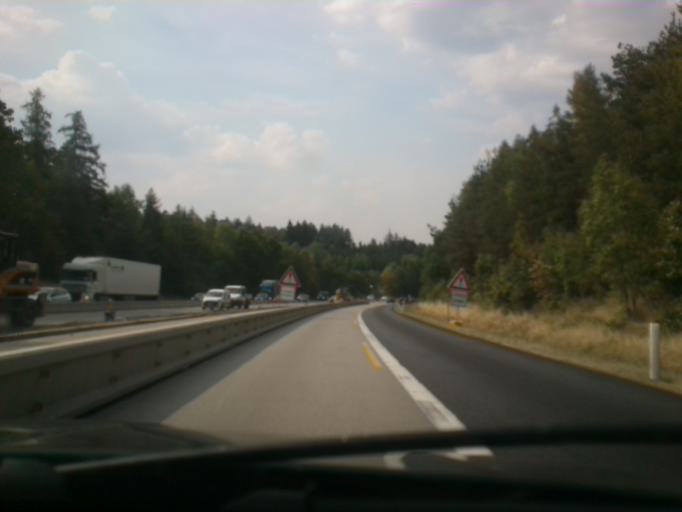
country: CZ
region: Central Bohemia
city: Ondrejov
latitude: 49.8436
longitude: 14.8010
